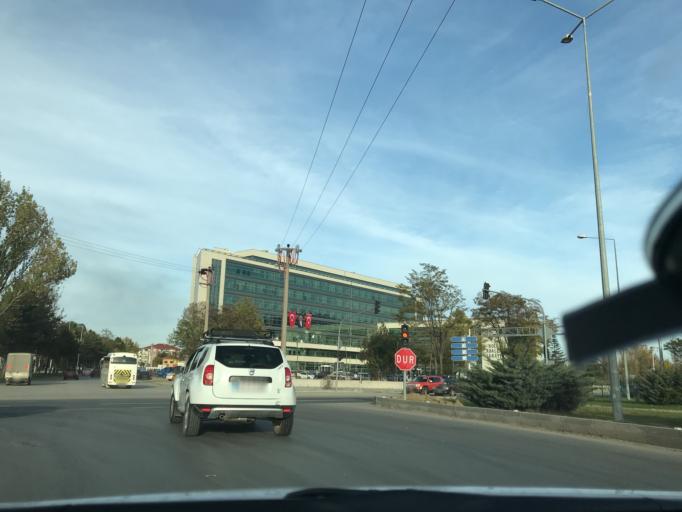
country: TR
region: Bolu
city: Bolu
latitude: 40.7372
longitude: 31.6198
